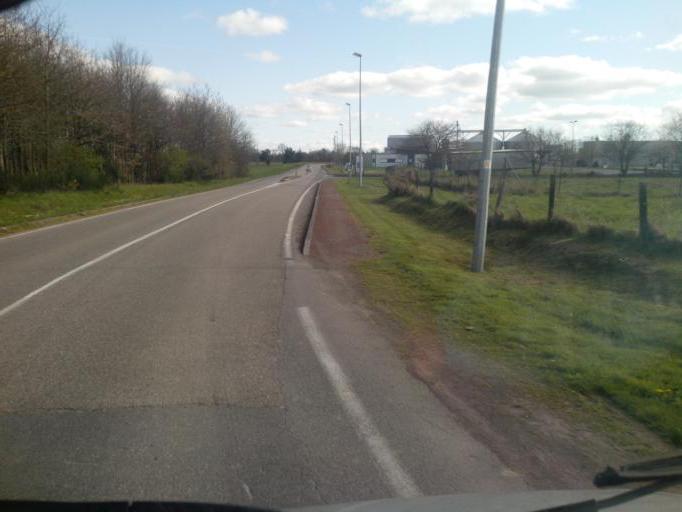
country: FR
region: Brittany
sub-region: Departement d'Ille-et-Vilaine
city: Plelan-le-Grand
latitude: 48.0029
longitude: -2.0848
